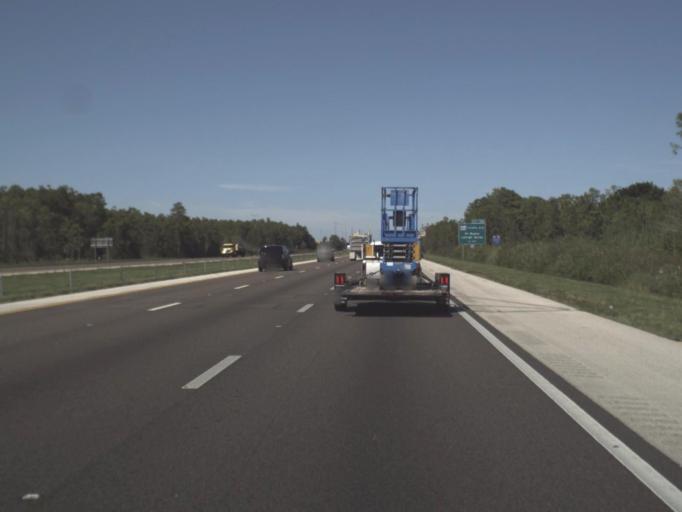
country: US
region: Florida
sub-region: Lee County
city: Fort Myers
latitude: 26.5980
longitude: -81.7987
